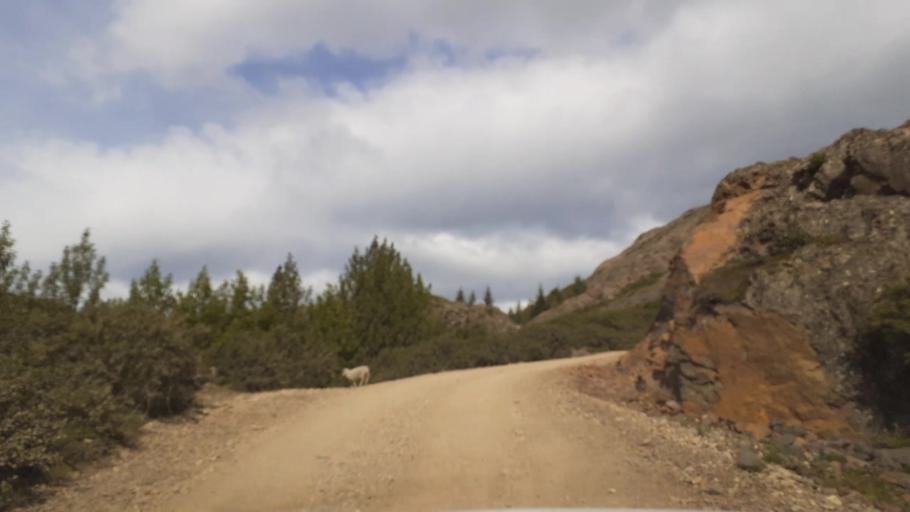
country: IS
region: East
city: Hoefn
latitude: 64.4380
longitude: -14.9120
